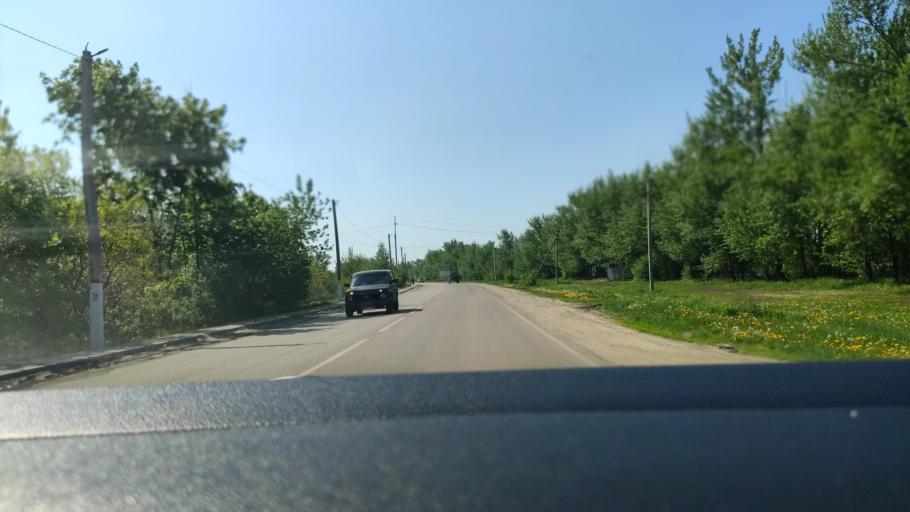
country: RU
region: Voronezj
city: Novaya Usman'
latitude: 51.6080
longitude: 39.3736
